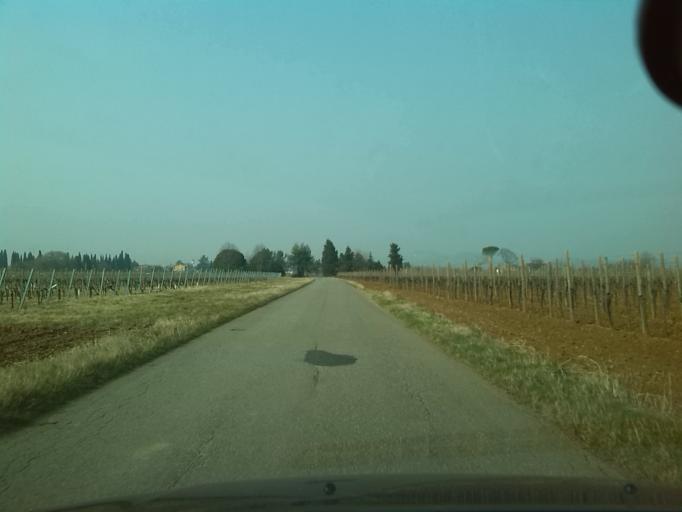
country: IT
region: Friuli Venezia Giulia
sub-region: Provincia di Gorizia
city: Moraro
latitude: 45.9133
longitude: 13.4866
